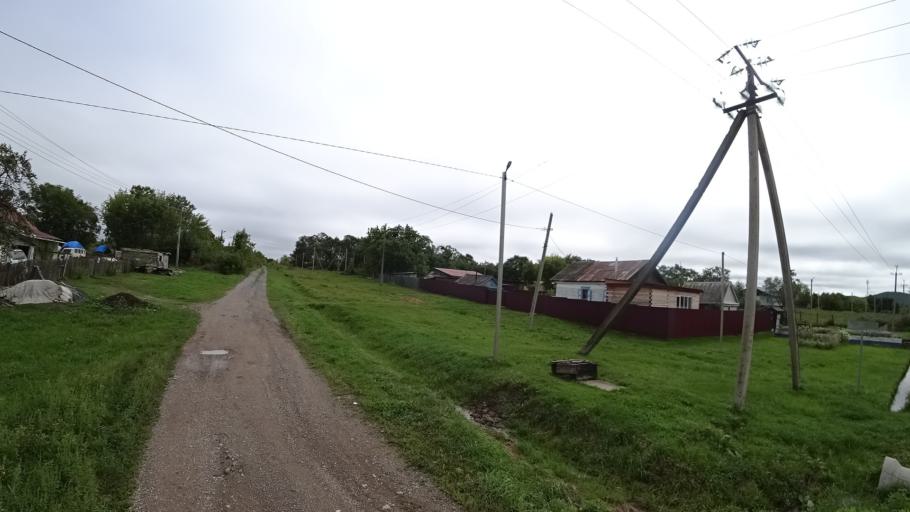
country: RU
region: Primorskiy
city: Lyalichi
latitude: 44.0789
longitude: 132.4776
